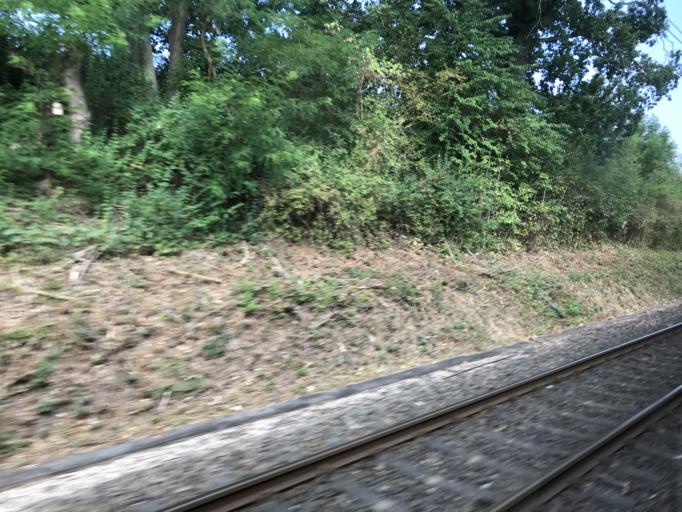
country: DE
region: Hesse
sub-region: Regierungsbezirk Darmstadt
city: Idstein
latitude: 50.2461
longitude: 8.2486
